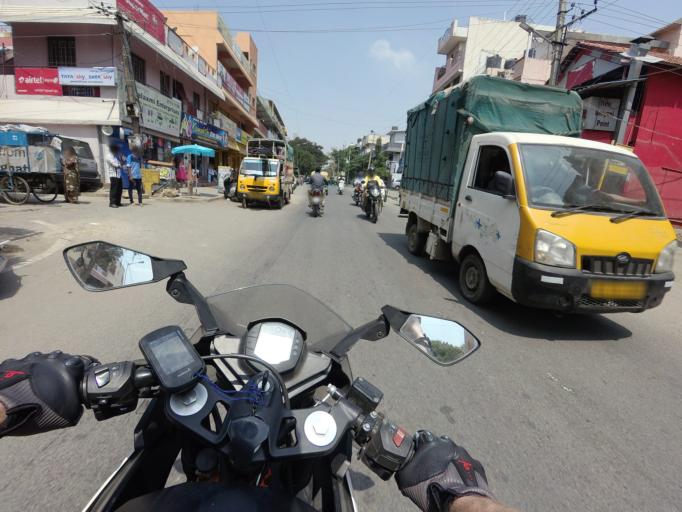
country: IN
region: Karnataka
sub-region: Bangalore Urban
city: Bangalore
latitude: 13.0141
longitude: 77.6411
